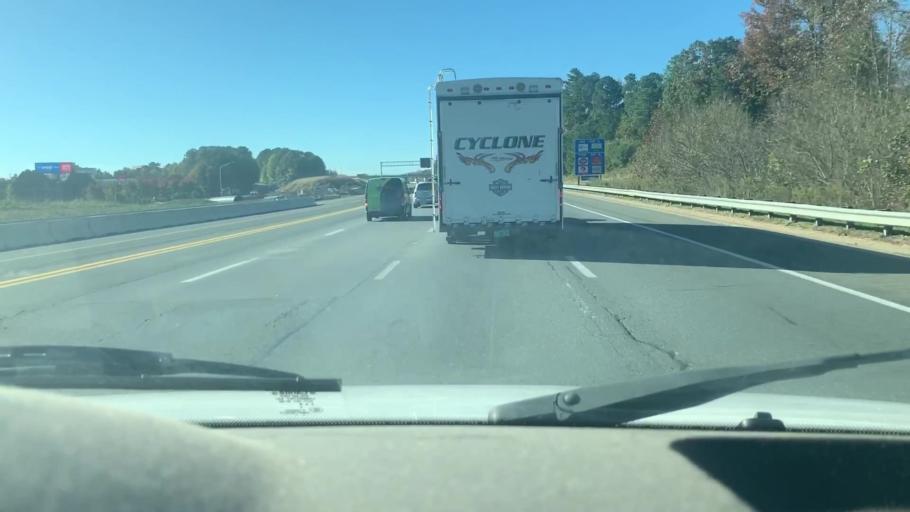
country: US
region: North Carolina
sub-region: Mecklenburg County
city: Huntersville
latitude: 35.3546
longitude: -80.8457
